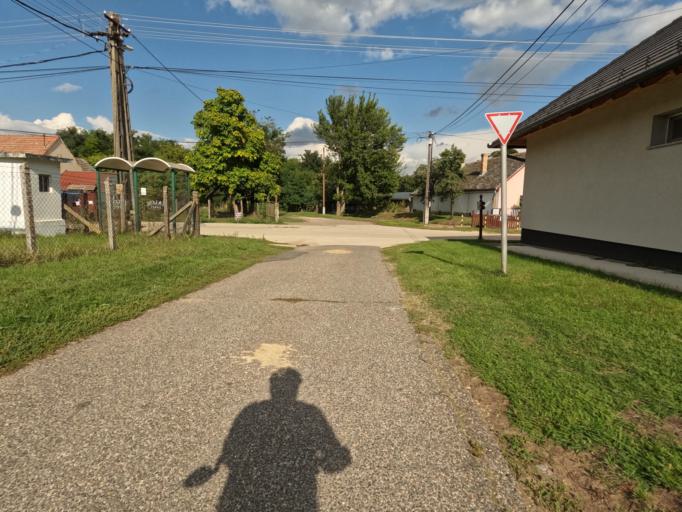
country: HU
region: Tolna
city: Tengelic
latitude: 46.5355
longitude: 18.7077
